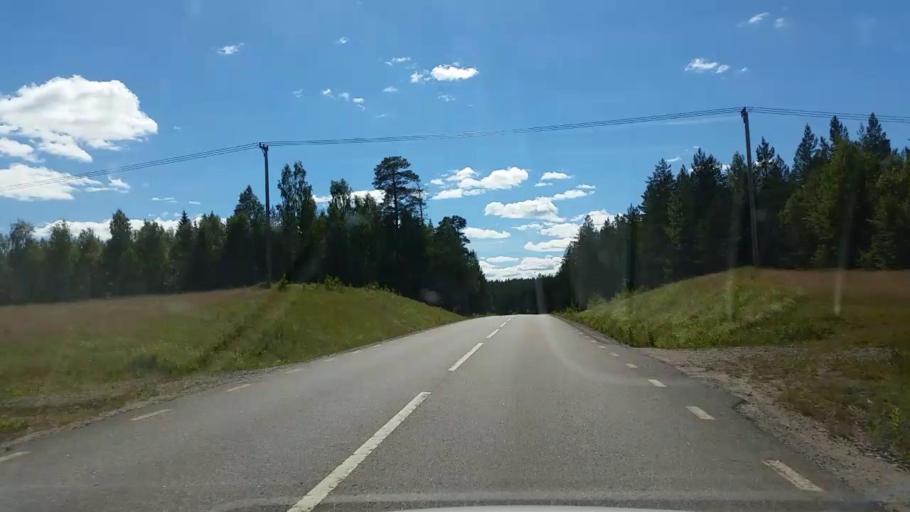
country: SE
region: Dalarna
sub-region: Faluns Kommun
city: Svardsjo
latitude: 61.0405
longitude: 15.7899
